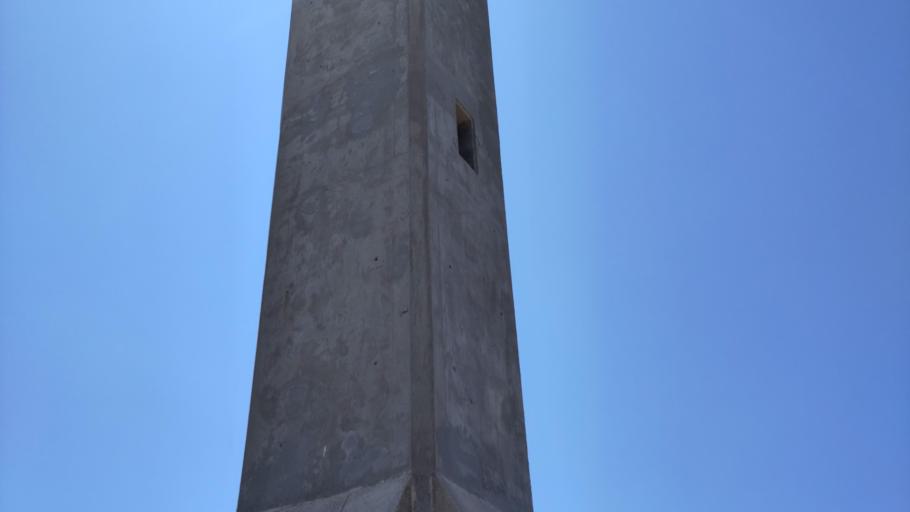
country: GR
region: South Aegean
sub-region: Nomos Dodekanisou
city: Kremasti
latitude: 36.3993
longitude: 28.1394
